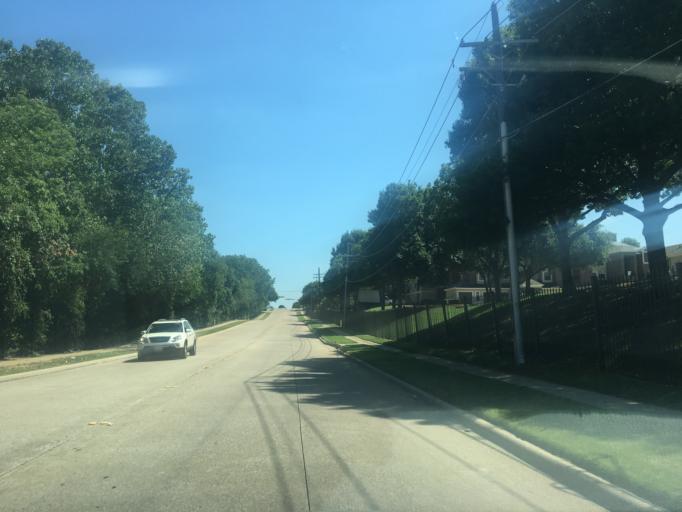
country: US
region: Texas
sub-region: Denton County
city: Lewisville
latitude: 33.0065
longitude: -96.9897
